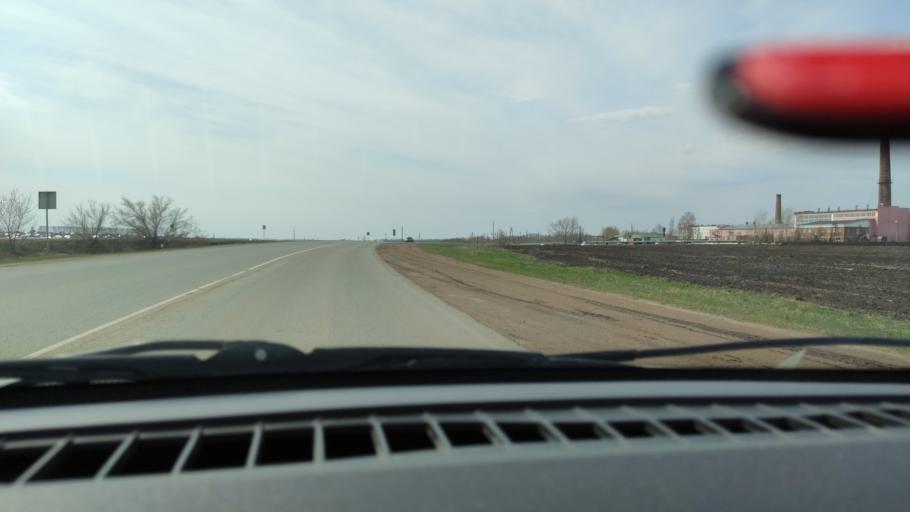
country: RU
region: Bashkortostan
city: Dyurtyuli
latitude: 55.4988
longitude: 54.8263
